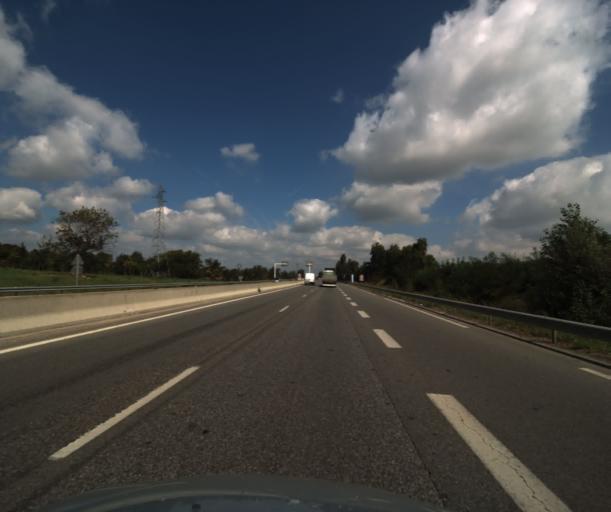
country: FR
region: Midi-Pyrenees
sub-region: Departement de la Haute-Garonne
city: Pinsaguel
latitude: 43.5060
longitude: 1.3848
